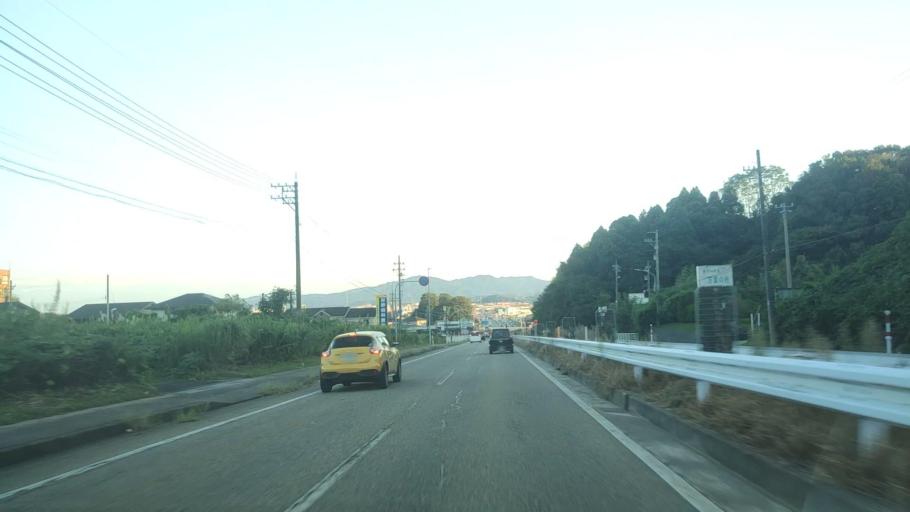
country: JP
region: Toyama
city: Himi
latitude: 36.8488
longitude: 136.9795
